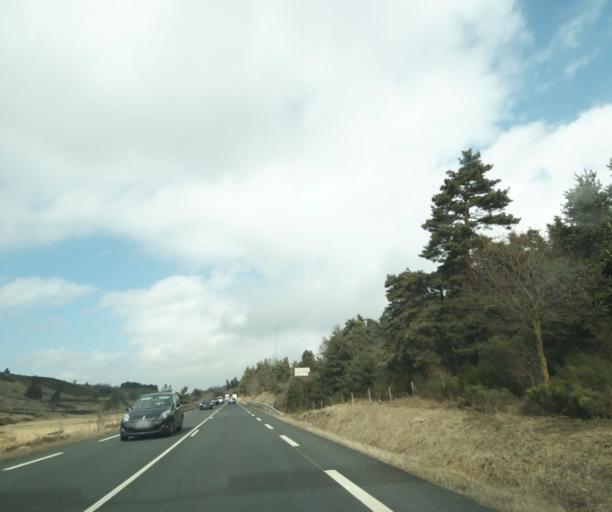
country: FR
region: Languedoc-Roussillon
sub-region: Departement de la Lozere
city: Mende
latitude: 44.6079
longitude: 3.6759
